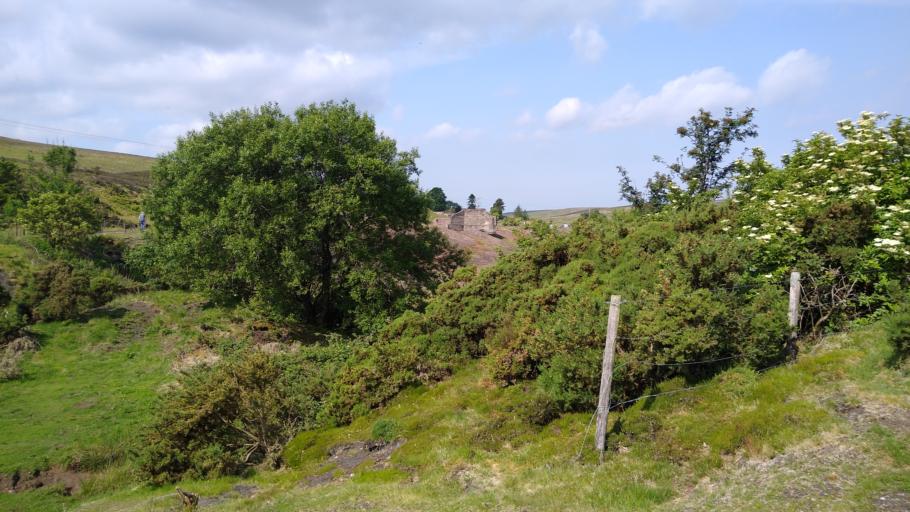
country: GB
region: England
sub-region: Northumberland
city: Greenhead
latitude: 54.9255
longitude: -2.5938
